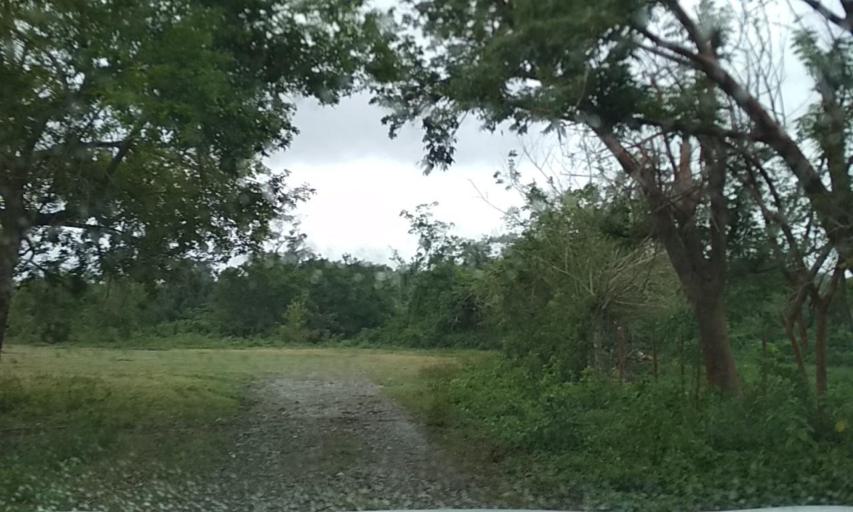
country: MX
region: Veracruz
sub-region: Papantla
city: El Chote
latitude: 20.3768
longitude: -97.3463
